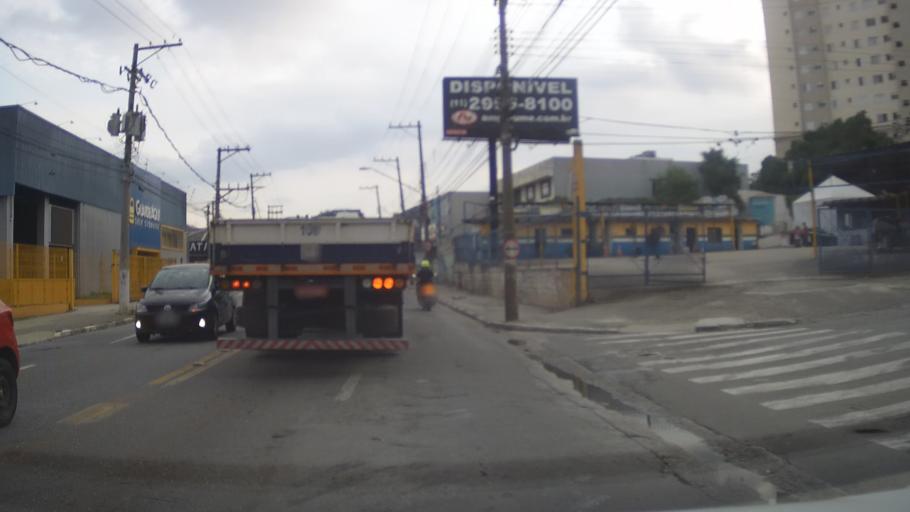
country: BR
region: Sao Paulo
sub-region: Guarulhos
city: Guarulhos
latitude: -23.4661
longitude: -46.5145
